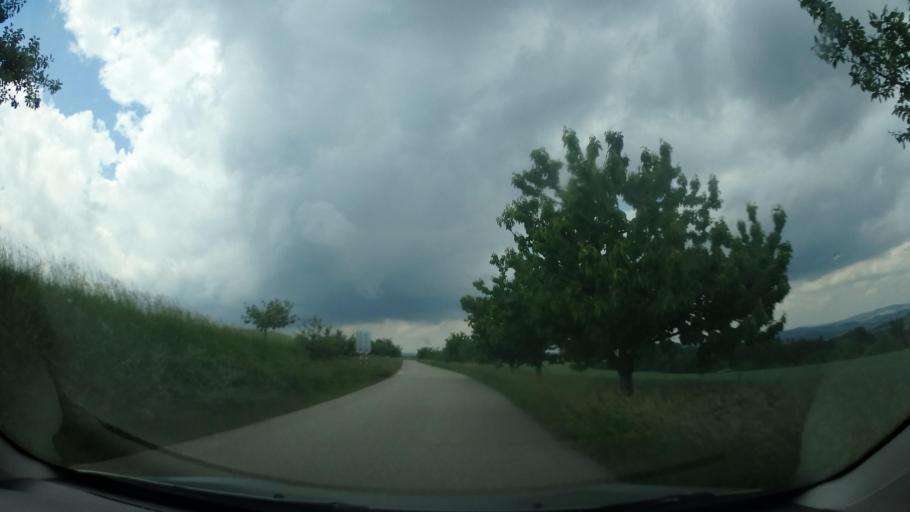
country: CZ
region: South Moravian
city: Boritov
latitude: 49.4548
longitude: 16.6008
